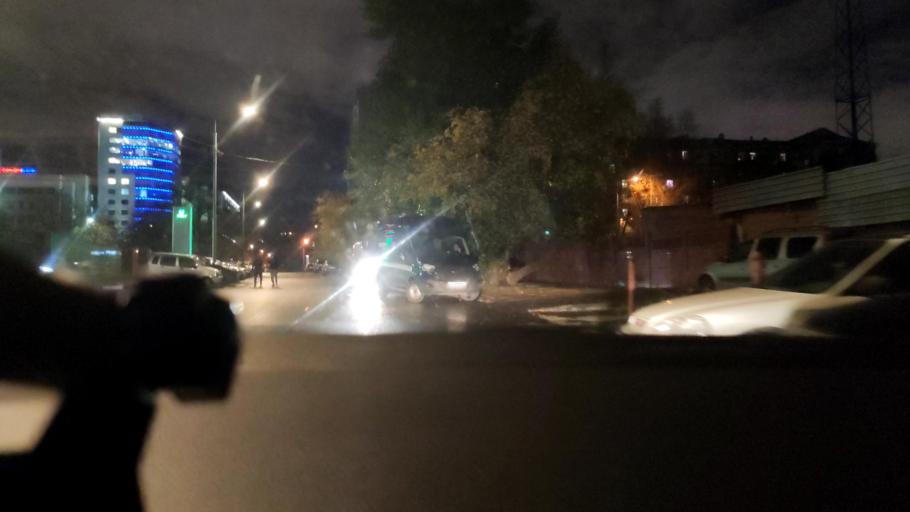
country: RU
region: Moscow
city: Novyye Cheremushki
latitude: 55.7004
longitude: 37.5816
